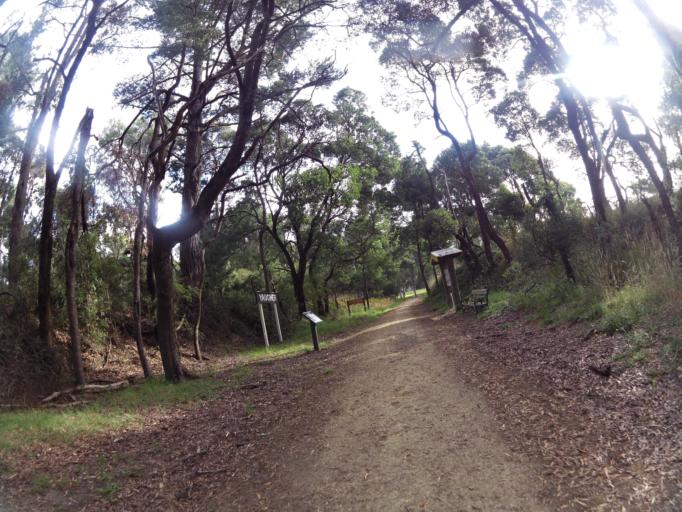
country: AU
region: Victoria
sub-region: Colac-Otway
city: Colac
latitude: -38.5046
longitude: 143.7238
